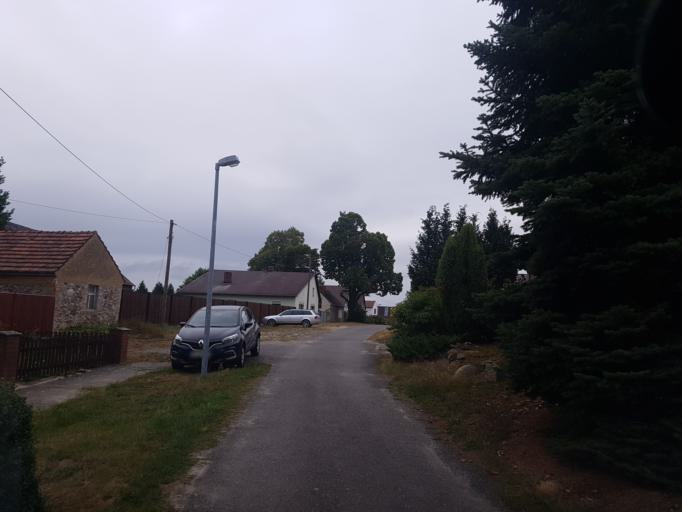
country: DE
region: Brandenburg
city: Crinitz
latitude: 51.7151
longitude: 13.8213
